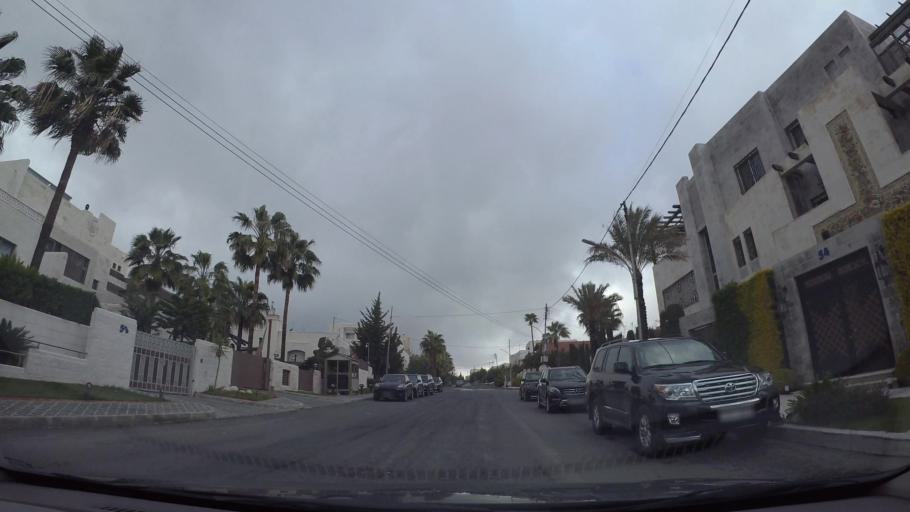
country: JO
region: Amman
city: Amman
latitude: 31.9491
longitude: 35.8979
